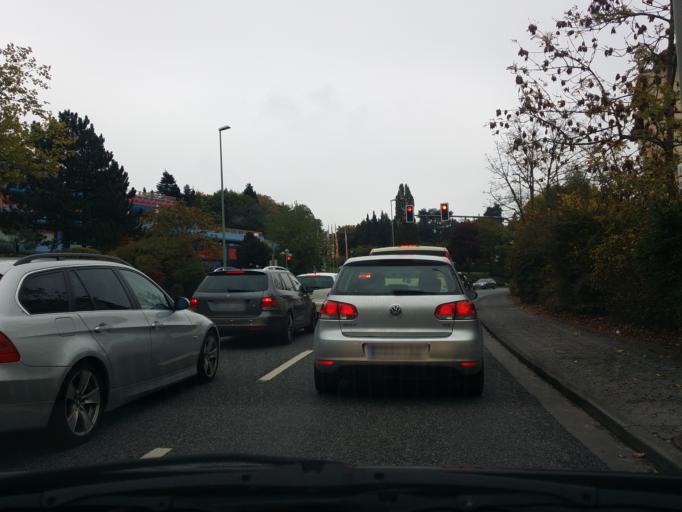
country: DE
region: Hesse
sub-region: Regierungsbezirk Darmstadt
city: Konigstein im Taunus
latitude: 50.1867
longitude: 8.4688
